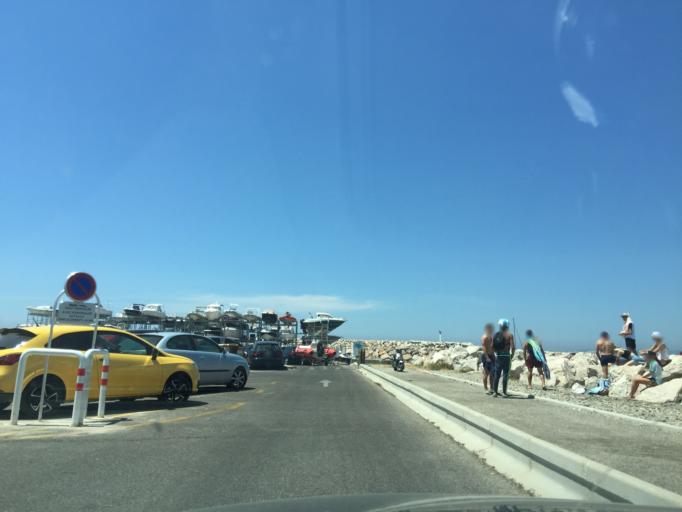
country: FR
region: Provence-Alpes-Cote d'Azur
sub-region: Departement des Bouches-du-Rhone
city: Marseille 08
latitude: 43.2452
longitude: 5.3664
